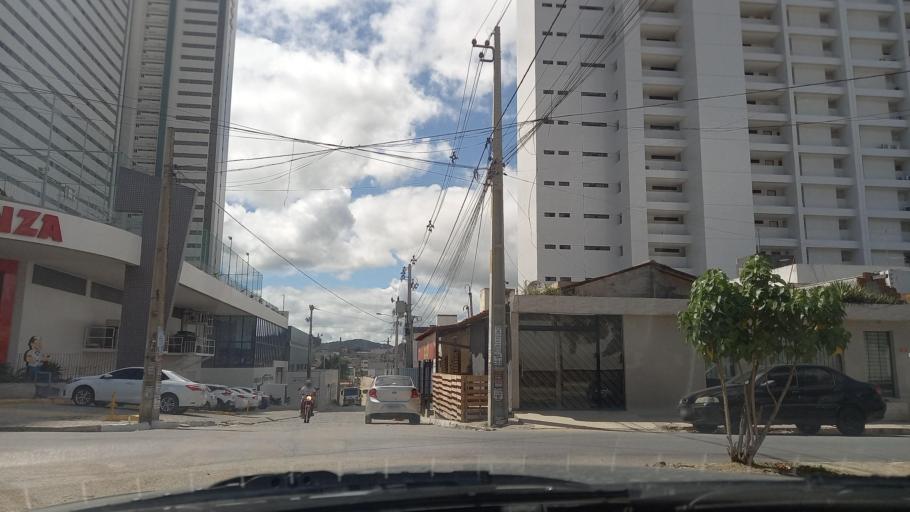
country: BR
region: Pernambuco
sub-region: Caruaru
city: Caruaru
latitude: -8.2657
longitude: -35.9644
